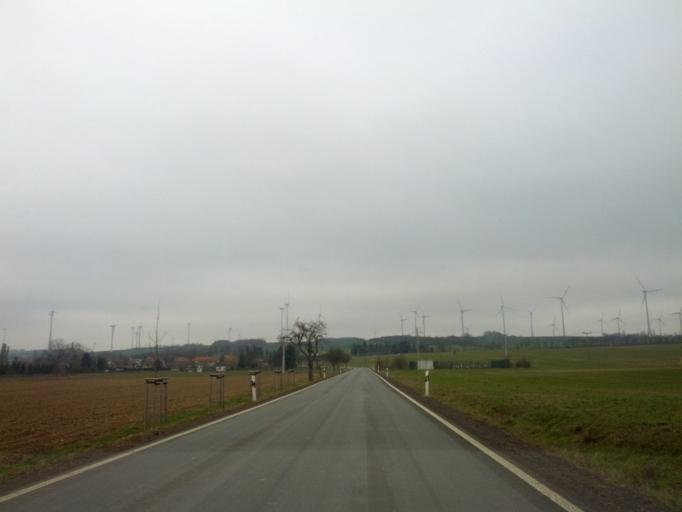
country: DE
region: Thuringia
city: Wangenheim
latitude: 51.0124
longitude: 10.6306
